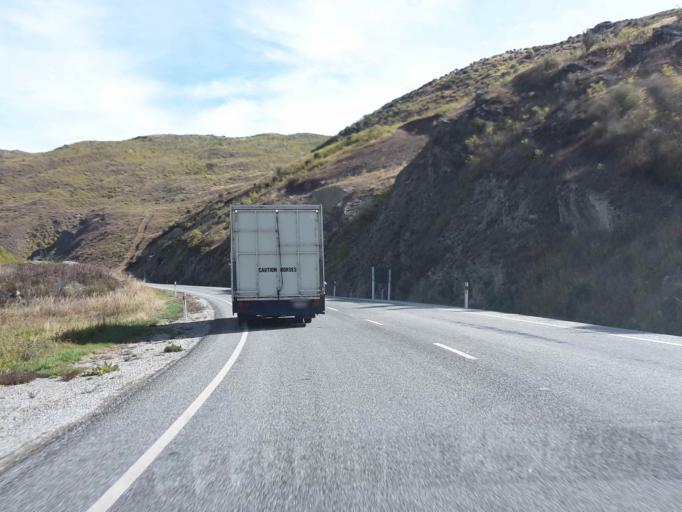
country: NZ
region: Otago
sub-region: Queenstown-Lakes District
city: Wanaka
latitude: -44.6962
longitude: 169.4946
